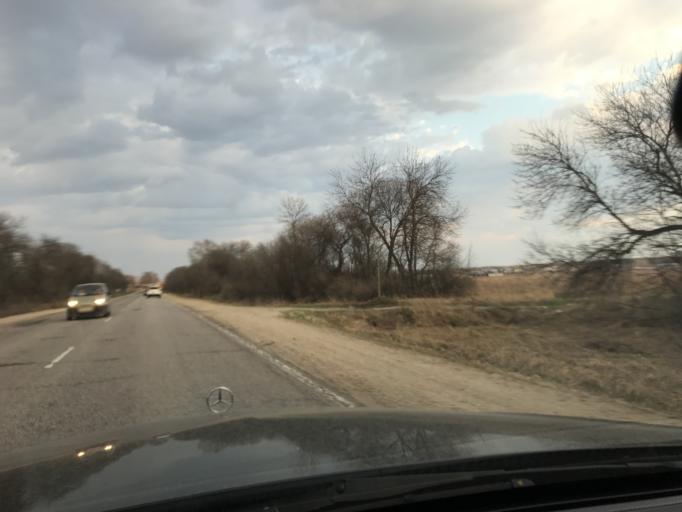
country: RU
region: Vladimir
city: Murom
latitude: 55.6180
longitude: 41.9315
